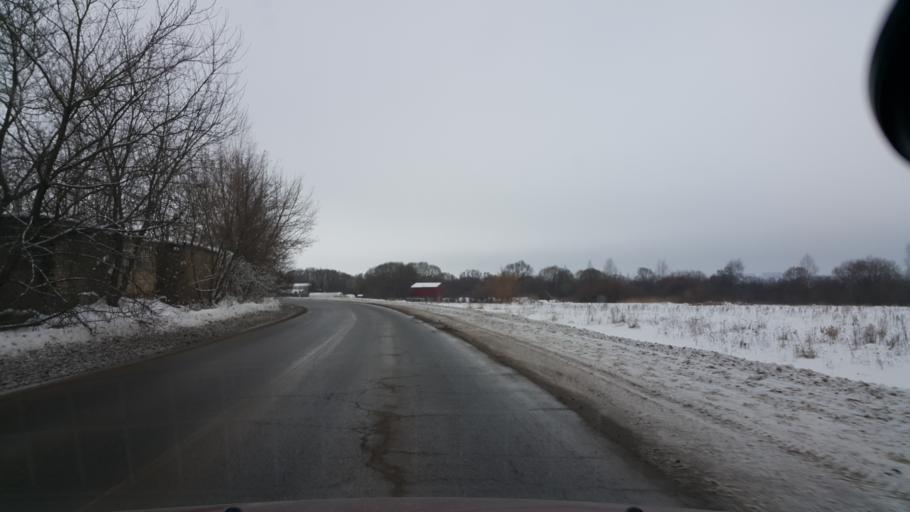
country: RU
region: Tambov
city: Pokrovo-Prigorodnoye
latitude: 52.6602
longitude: 41.4362
